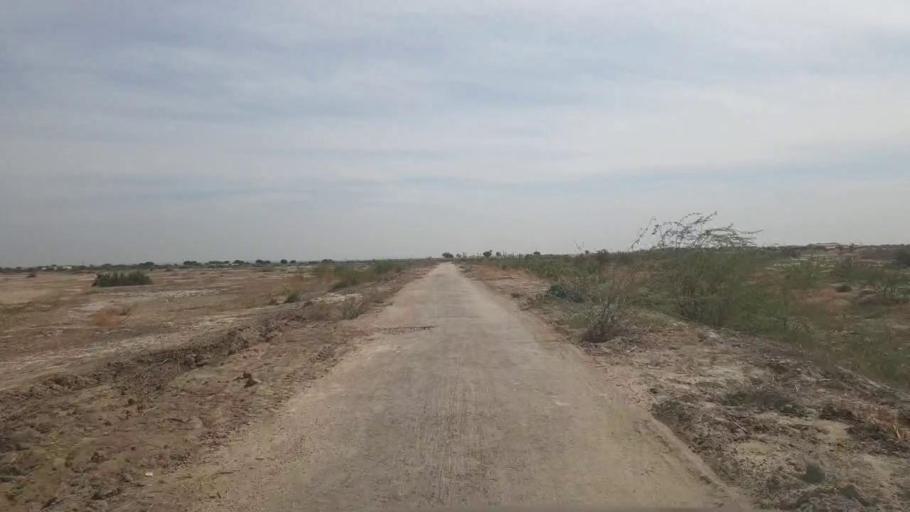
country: PK
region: Sindh
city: Kunri
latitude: 25.2159
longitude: 69.6227
